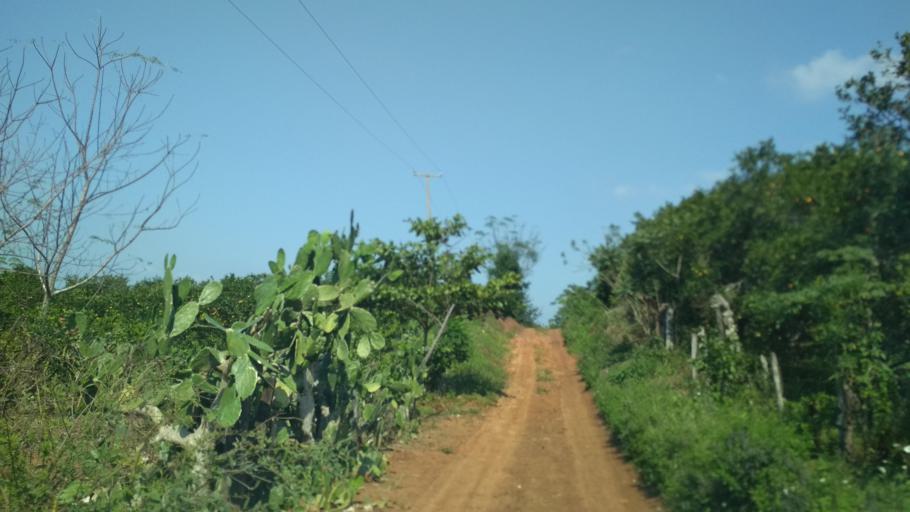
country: MX
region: Puebla
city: San Jose Acateno
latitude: 20.1761
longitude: -97.2278
